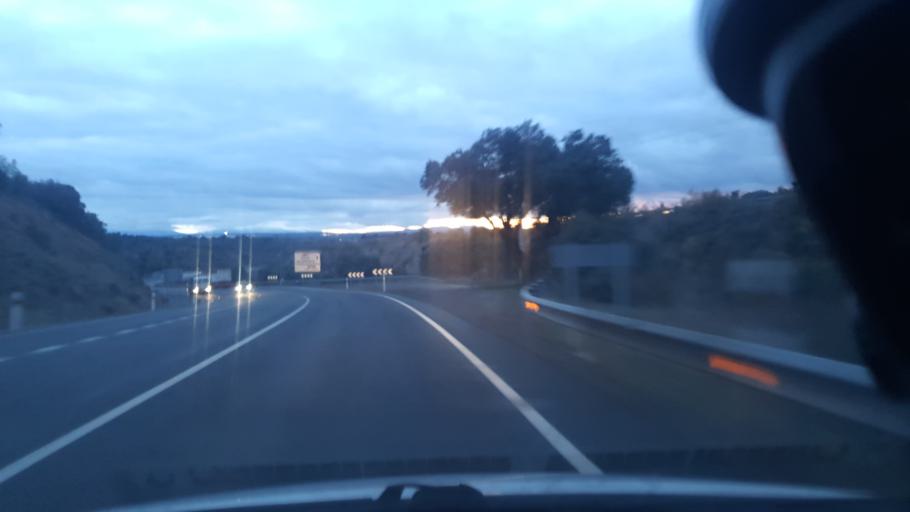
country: ES
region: Castille and Leon
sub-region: Provincia de Avila
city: Ojos-Albos
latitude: 40.7210
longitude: -4.5294
